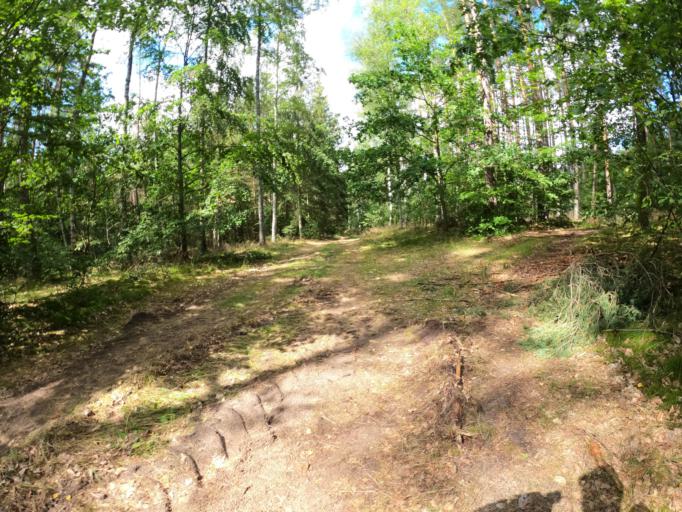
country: PL
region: West Pomeranian Voivodeship
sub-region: Powiat bialogardzki
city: Tychowo
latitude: 54.0126
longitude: 16.3550
